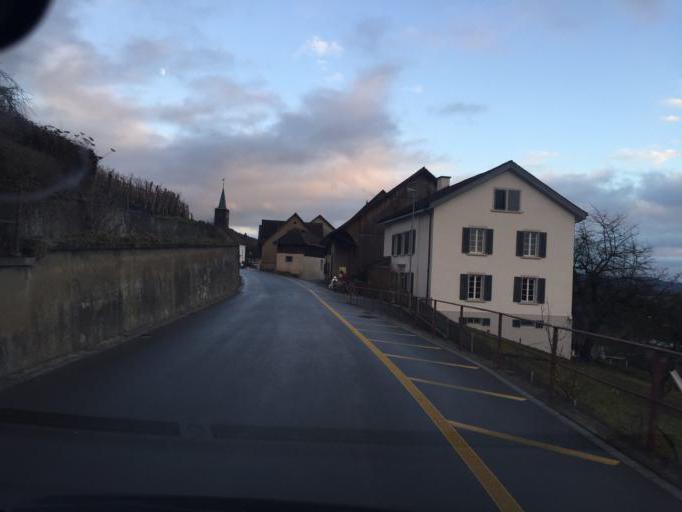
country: DE
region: Baden-Wuerttemberg
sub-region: Freiburg Region
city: Busingen
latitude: 47.7065
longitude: 8.7202
